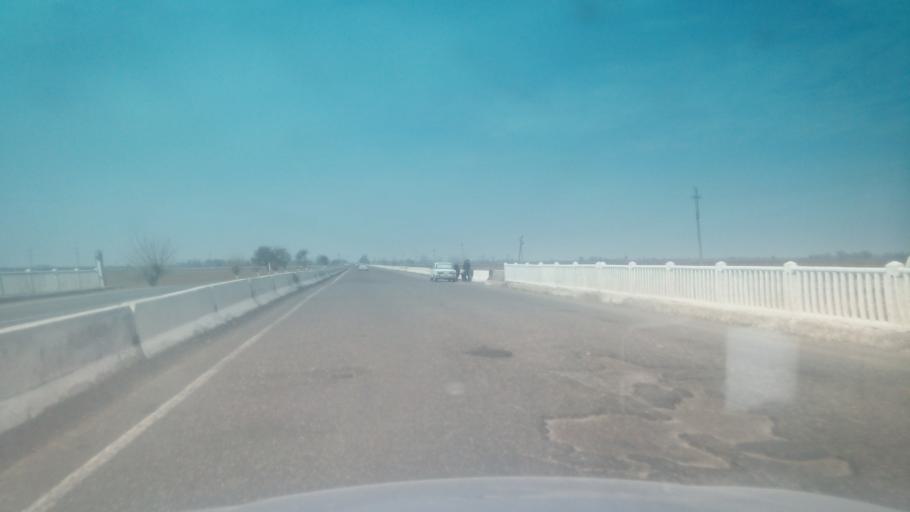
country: KZ
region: Ongtustik Qazaqstan
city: Myrzakent
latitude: 40.5194
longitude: 68.4696
